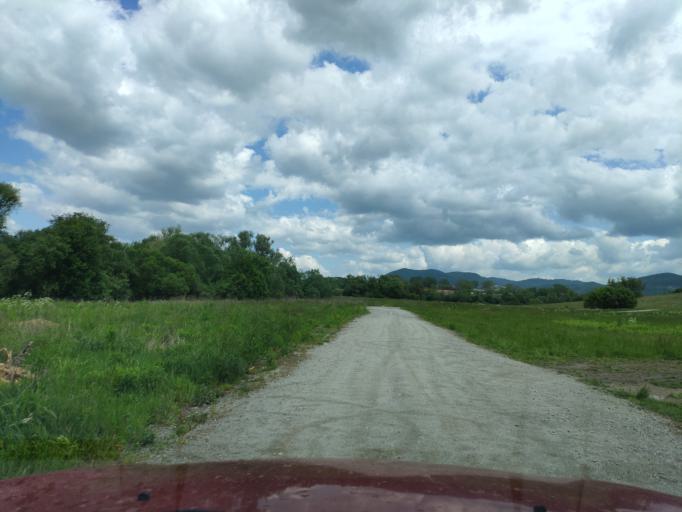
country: SK
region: Kosicky
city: Kosice
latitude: 48.8374
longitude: 21.3181
